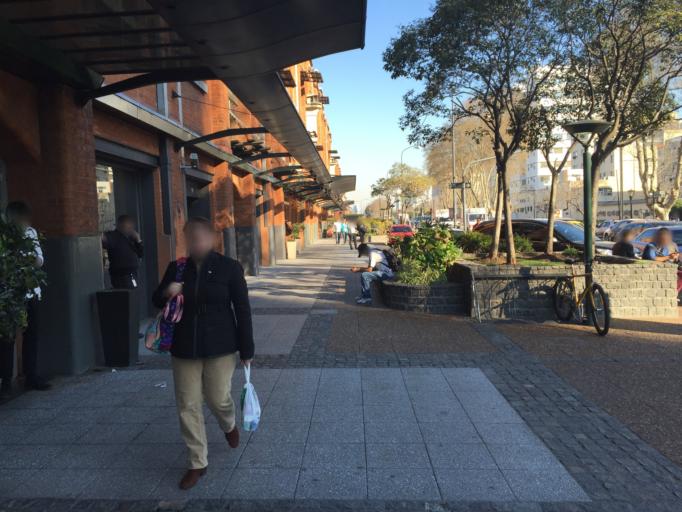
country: AR
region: Buenos Aires F.D.
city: Buenos Aires
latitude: -34.6025
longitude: -58.3672
